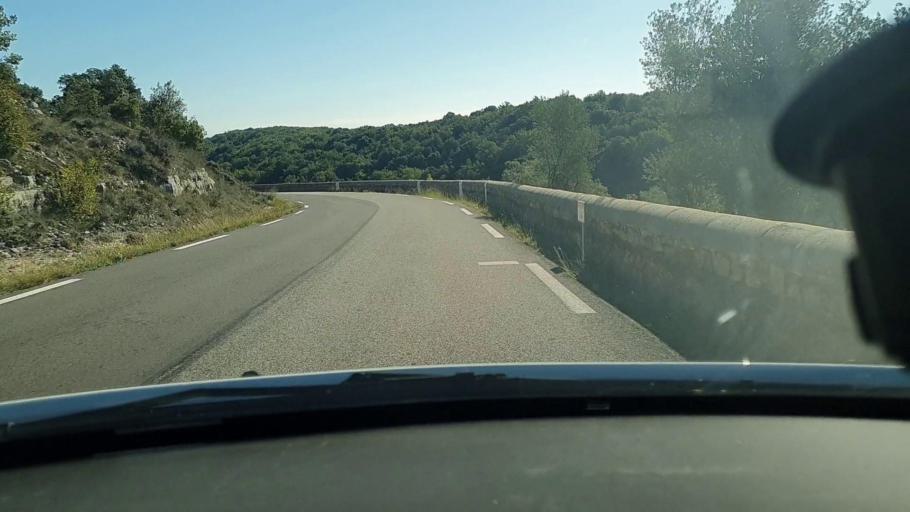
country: FR
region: Languedoc-Roussillon
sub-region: Departement du Gard
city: Goudargues
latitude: 44.2913
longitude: 4.4806
